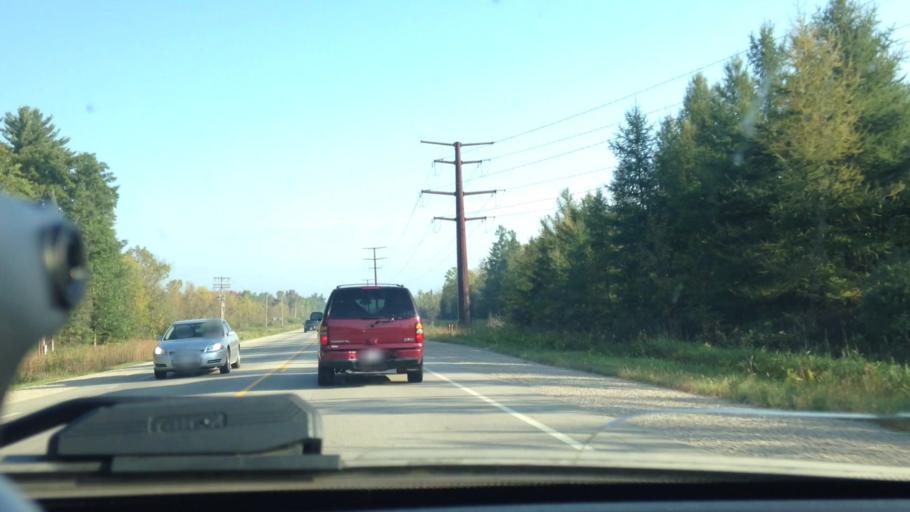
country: US
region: Wisconsin
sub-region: Marinette County
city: Peshtigo
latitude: 45.1775
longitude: -87.9958
